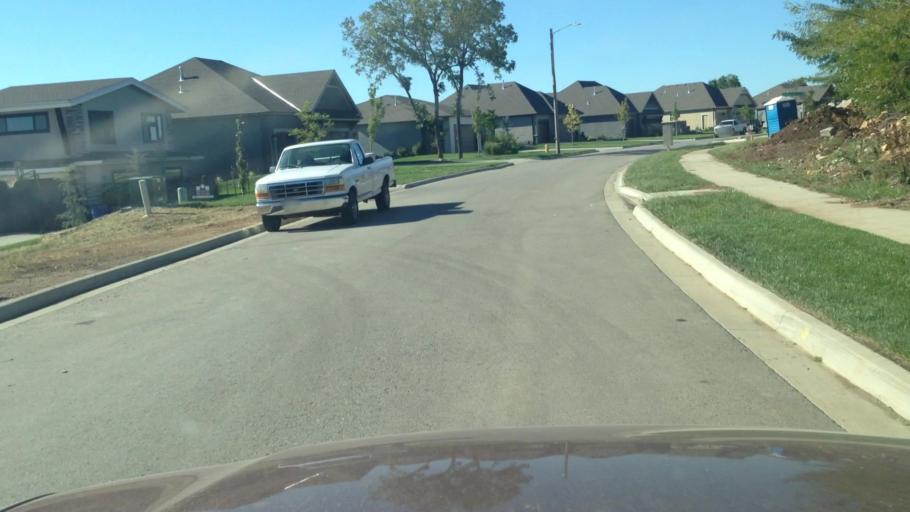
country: US
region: Kansas
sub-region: Douglas County
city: Lawrence
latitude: 38.9600
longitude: -95.3209
